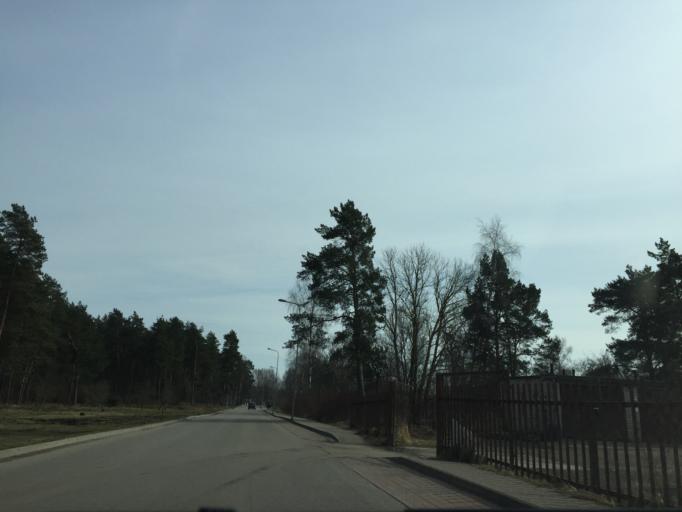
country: LV
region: Kekava
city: Balozi
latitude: 56.8755
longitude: 24.1251
